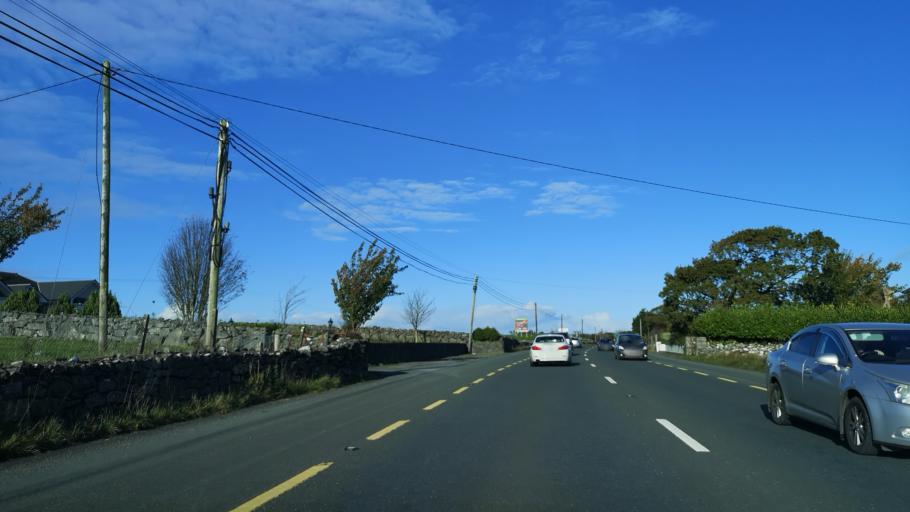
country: IE
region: Connaught
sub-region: County Galway
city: Moycullen
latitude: 53.4565
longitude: -9.0988
